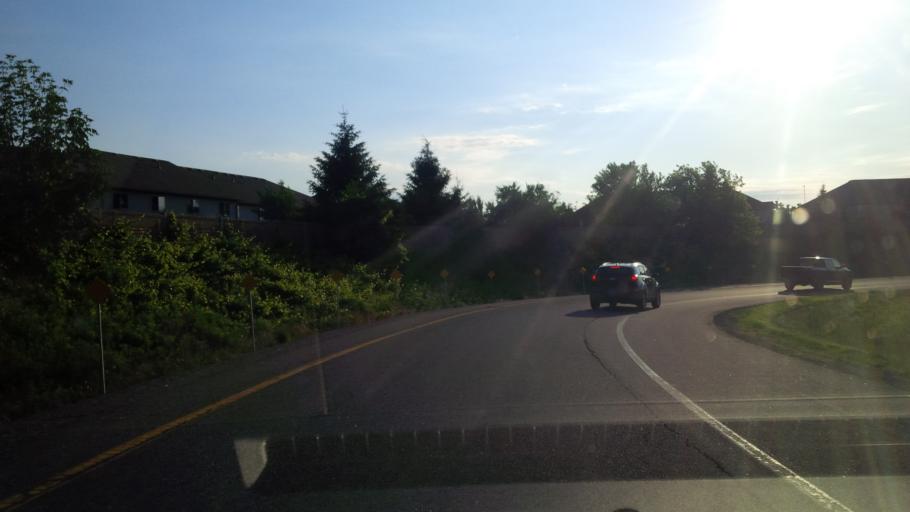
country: CA
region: Ontario
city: Ancaster
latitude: 43.2041
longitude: -79.9840
